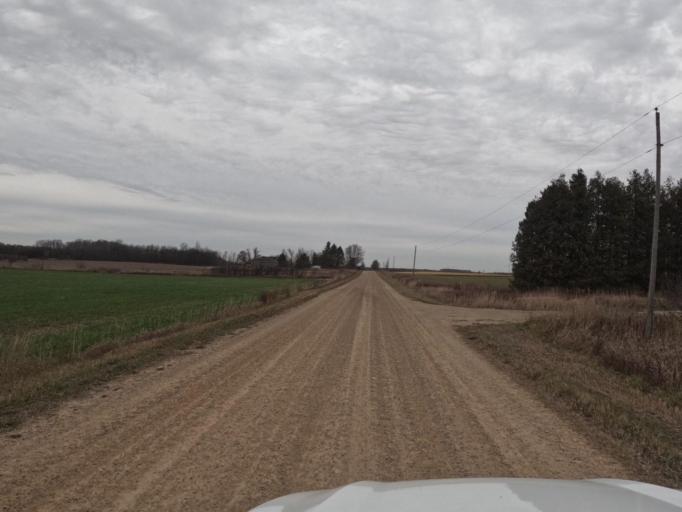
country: CA
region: Ontario
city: Shelburne
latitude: 44.0234
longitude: -80.3696
